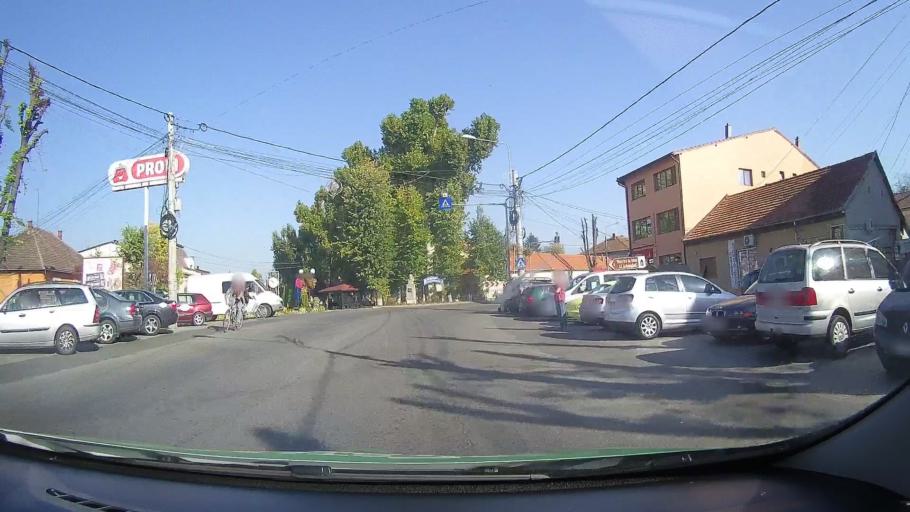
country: RO
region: Timis
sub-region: Comuna Faget
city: Faget
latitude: 45.8556
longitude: 22.1768
